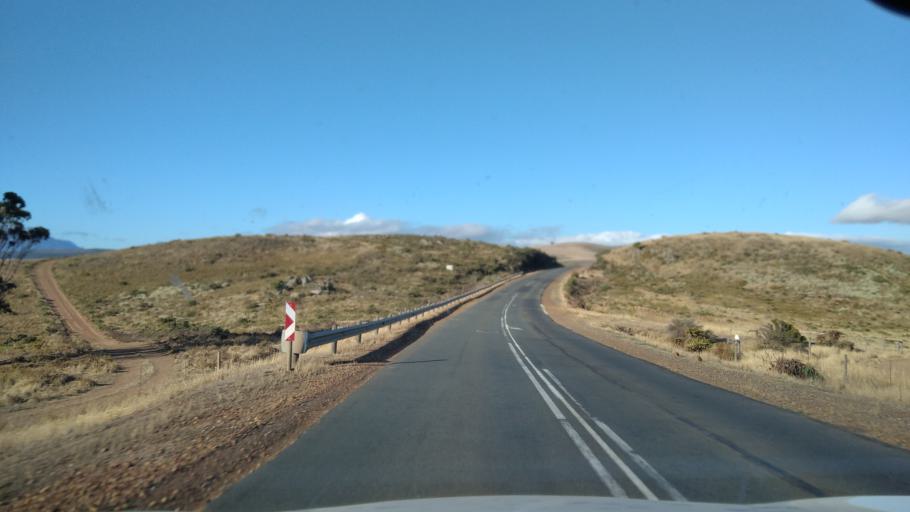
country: ZA
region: Western Cape
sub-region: Overberg District Municipality
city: Caledon
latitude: -34.1782
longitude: 19.2785
